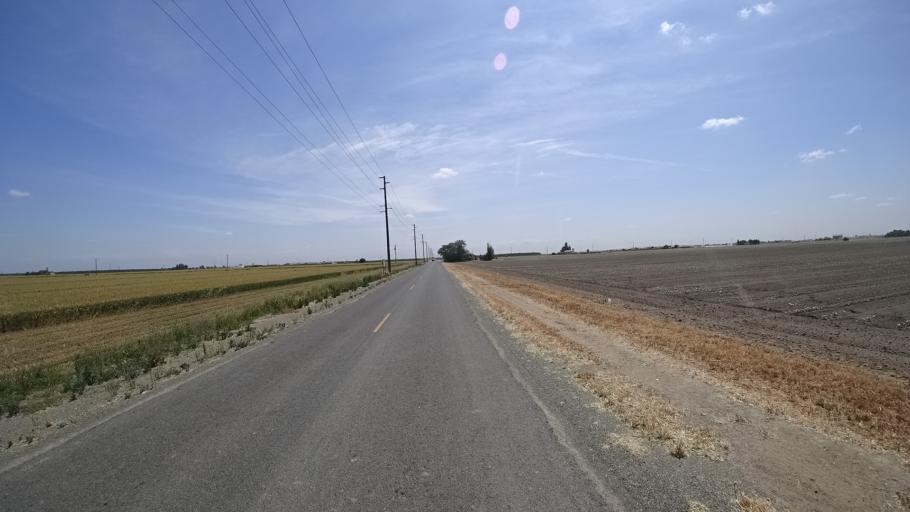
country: US
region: California
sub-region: Tulare County
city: Goshen
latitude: 36.3137
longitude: -119.5001
